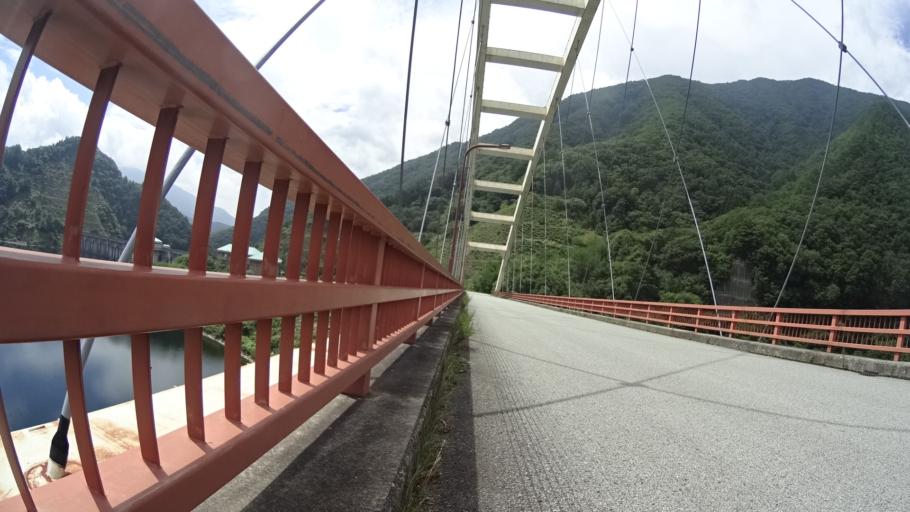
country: JP
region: Yamanashi
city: Nirasaki
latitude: 35.8621
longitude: 138.4982
